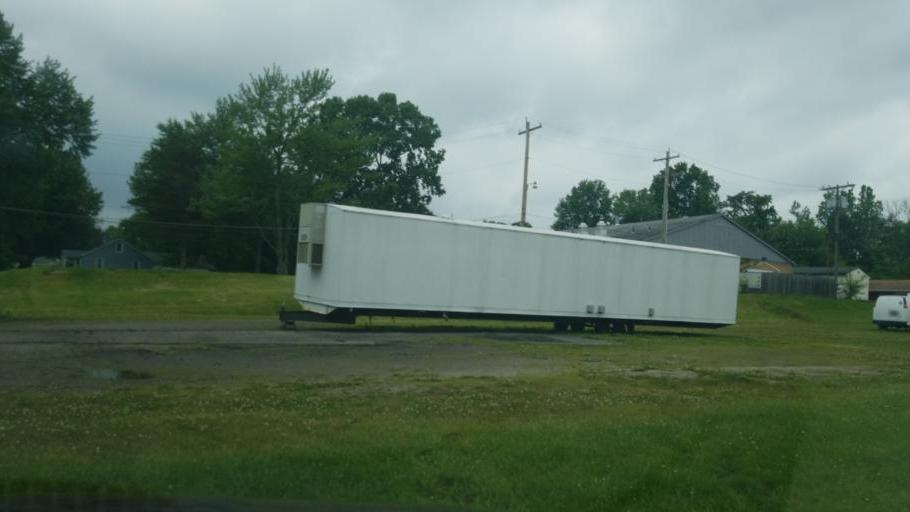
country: US
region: Ohio
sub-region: Crawford County
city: Galion
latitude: 40.7377
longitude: -82.7702
